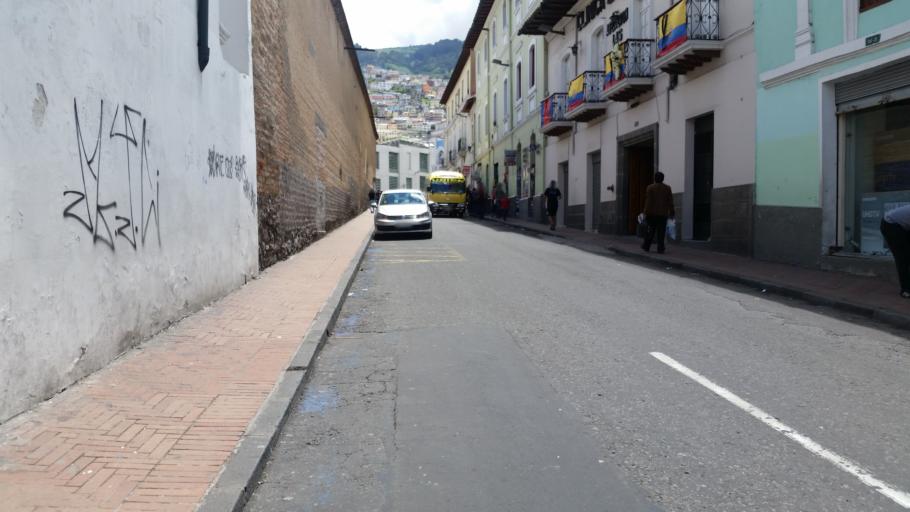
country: EC
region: Pichincha
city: Quito
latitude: -0.2175
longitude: -78.5136
